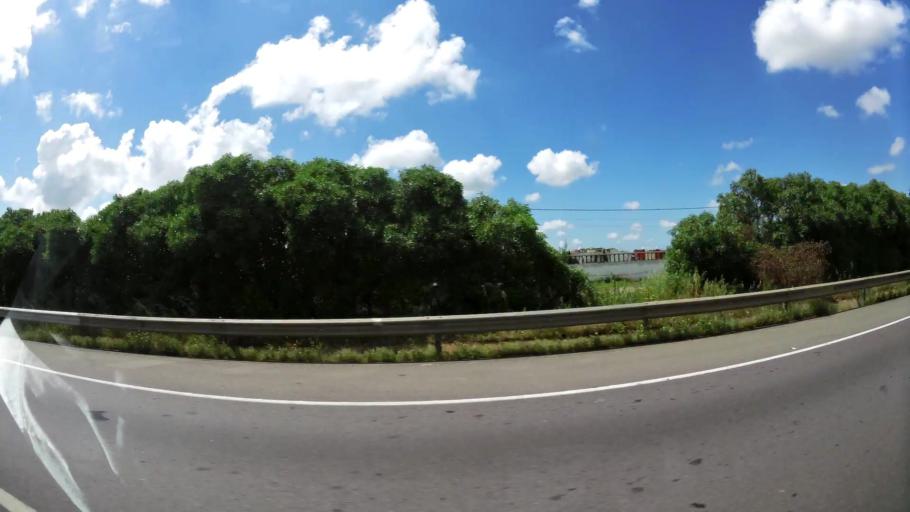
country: MA
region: Grand Casablanca
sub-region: Nouaceur
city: Bouskoura
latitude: 33.4508
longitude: -7.6336
